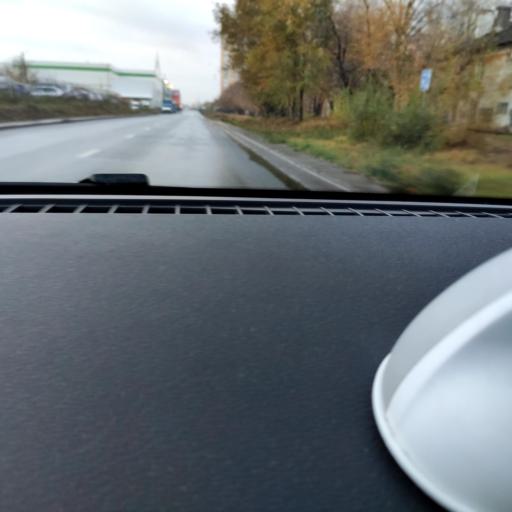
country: RU
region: Samara
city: Samara
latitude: 53.2097
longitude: 50.1937
